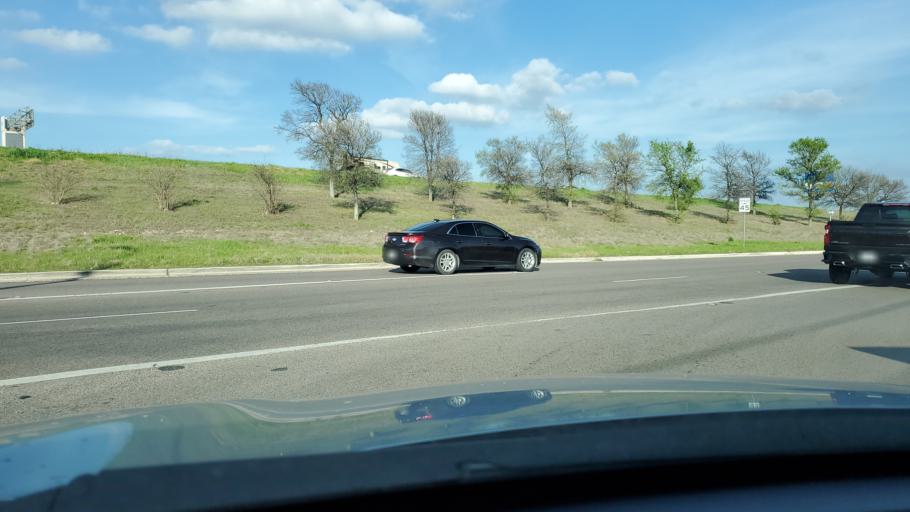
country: US
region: Texas
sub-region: Bell County
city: Killeen
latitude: 31.0902
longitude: -97.7200
